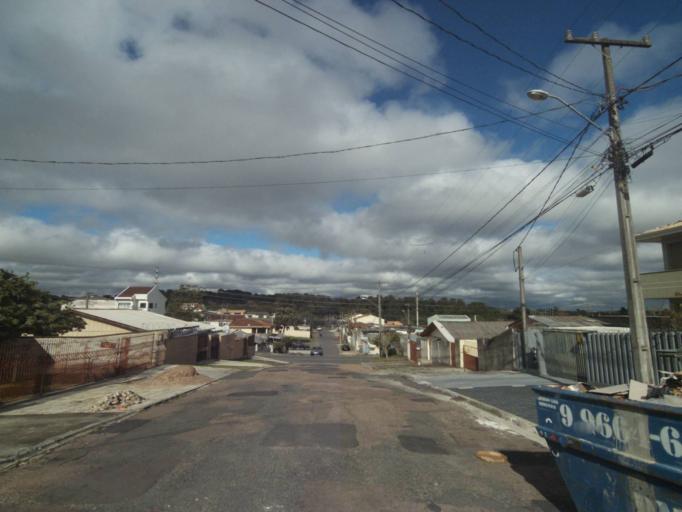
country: BR
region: Parana
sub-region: Sao Jose Dos Pinhais
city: Sao Jose dos Pinhais
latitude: -25.5207
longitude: -49.3031
